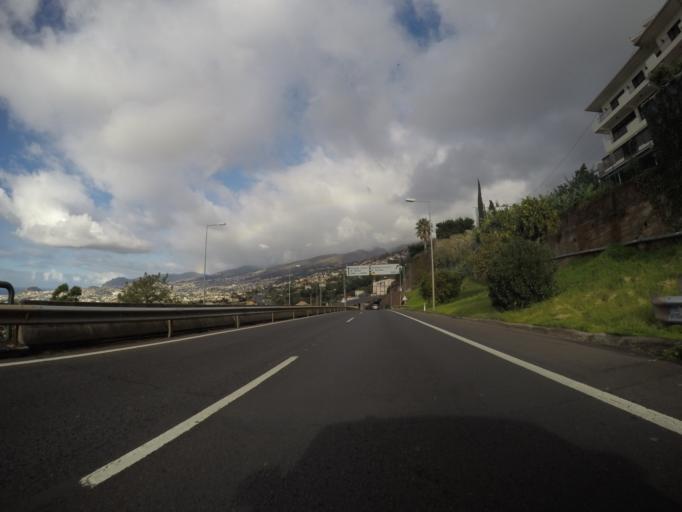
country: PT
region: Madeira
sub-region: Funchal
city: Nossa Senhora do Monte
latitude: 32.6530
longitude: -16.8774
